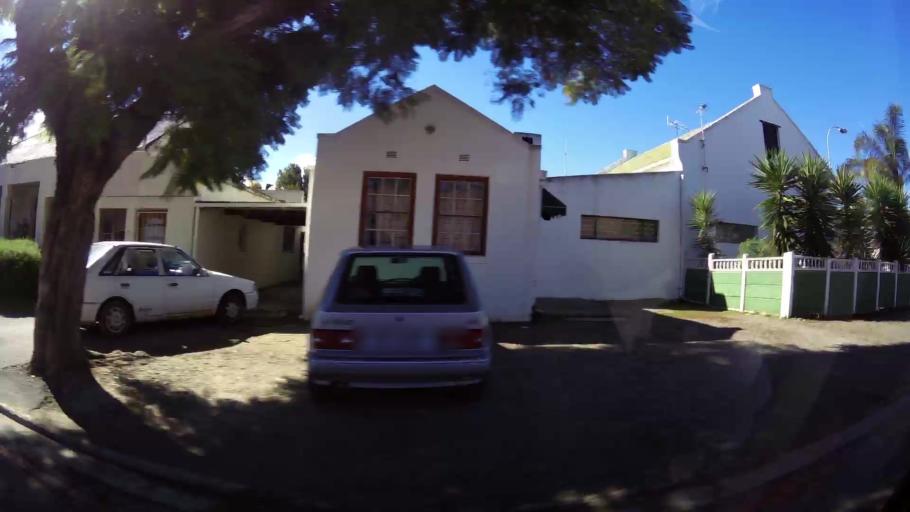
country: ZA
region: Western Cape
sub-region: Cape Winelands District Municipality
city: Ashton
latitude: -33.8061
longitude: 19.8777
